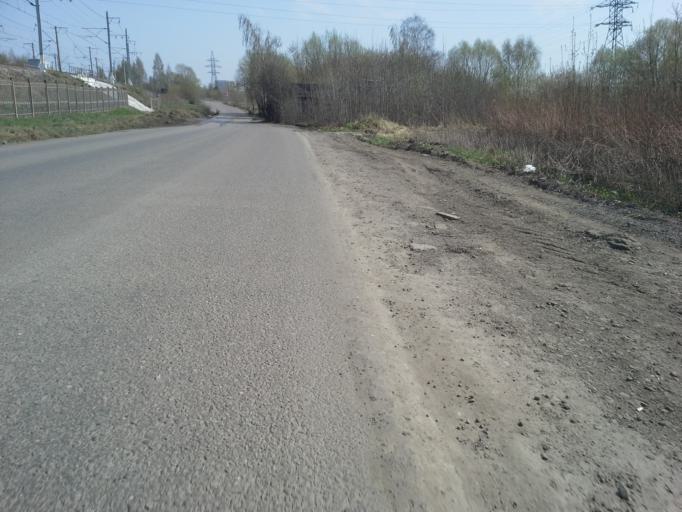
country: RU
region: Moskovskaya
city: Shcherbinka
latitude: 55.5148
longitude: 37.5393
